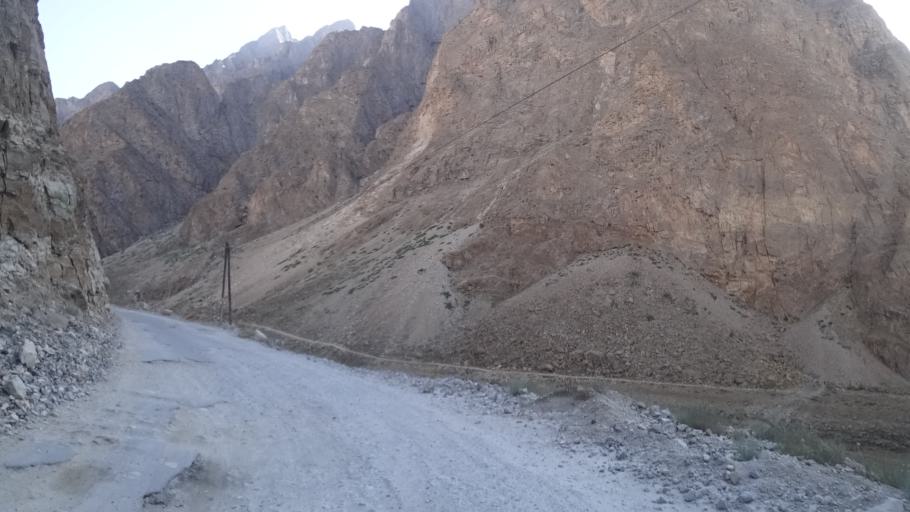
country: TJ
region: Gorno-Badakhshan
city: Rushon
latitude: 37.9891
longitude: 71.2692
